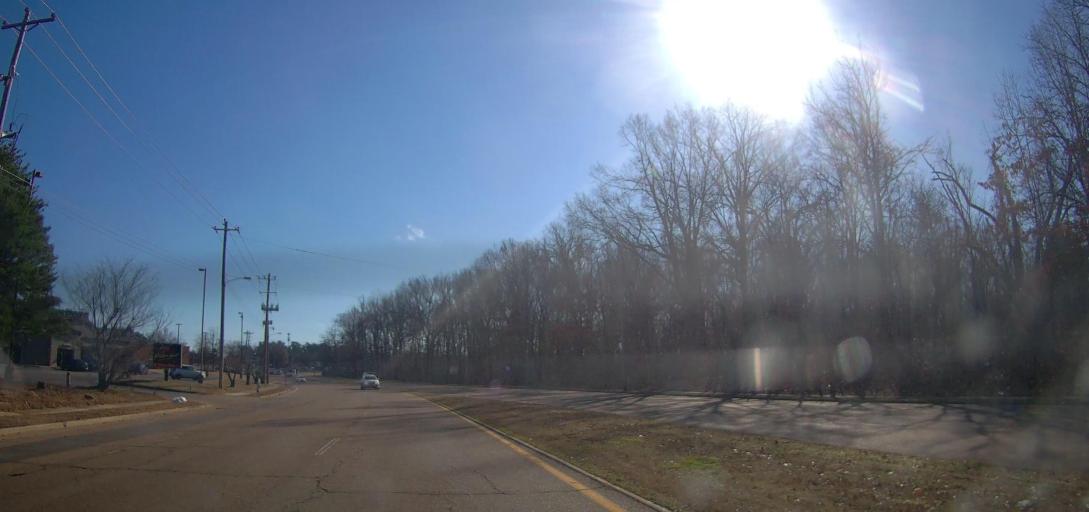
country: US
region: Tennessee
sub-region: Shelby County
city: Bartlett
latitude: 35.2371
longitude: -89.8971
